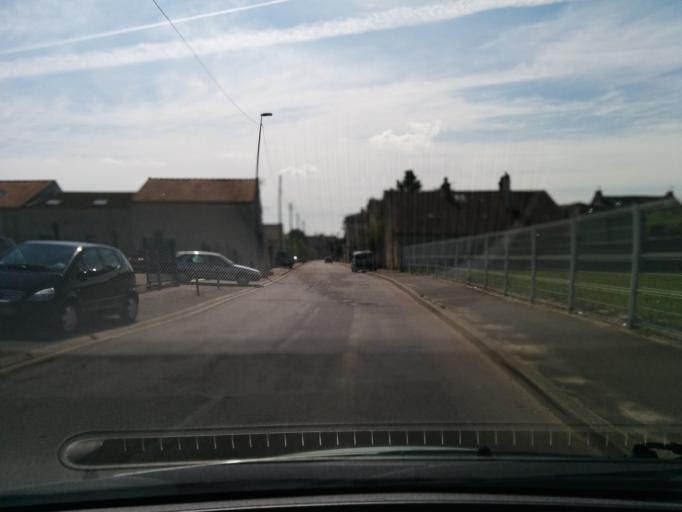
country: FR
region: Ile-de-France
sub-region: Departement des Yvelines
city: Mantes-la-Jolie
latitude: 48.9964
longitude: 1.7114
